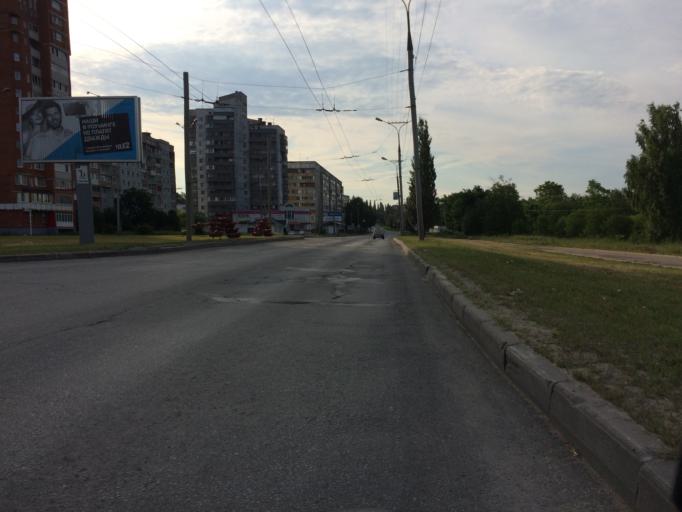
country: RU
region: Mariy-El
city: Yoshkar-Ola
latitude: 56.6237
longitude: 47.9330
